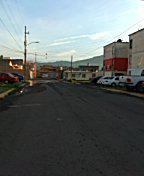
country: MX
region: Nayarit
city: Tepic
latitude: 21.4835
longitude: -104.8540
